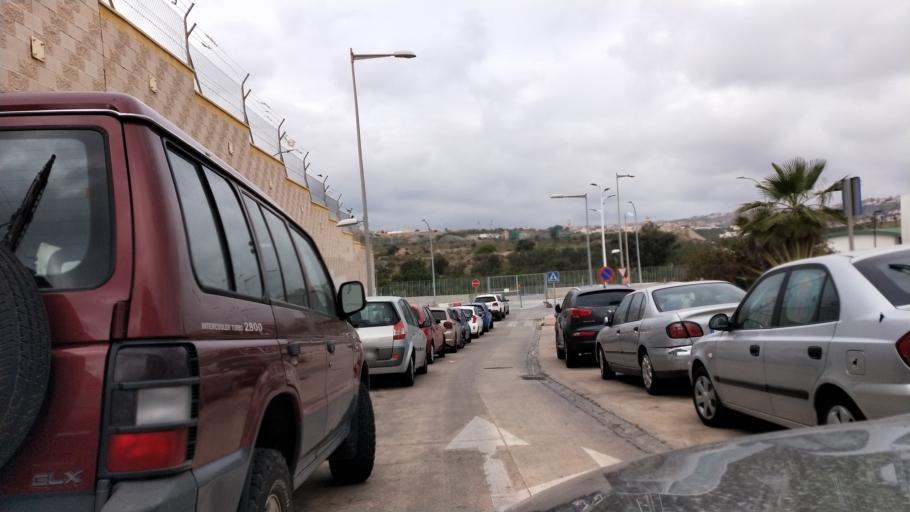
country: ES
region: Melilla
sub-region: Melilla
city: Melilla
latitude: 35.2871
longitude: -2.9551
